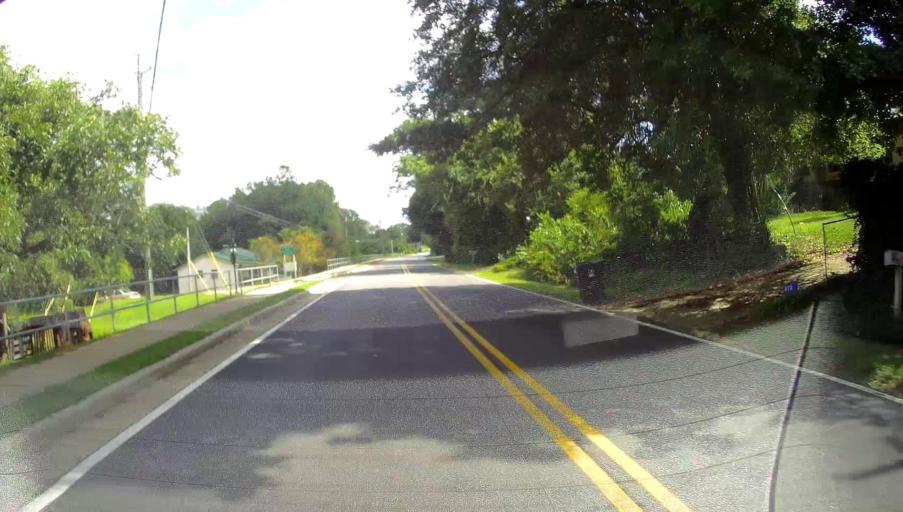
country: US
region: Georgia
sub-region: Chattahoochee County
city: Cusseta
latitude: 32.3016
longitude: -84.7714
